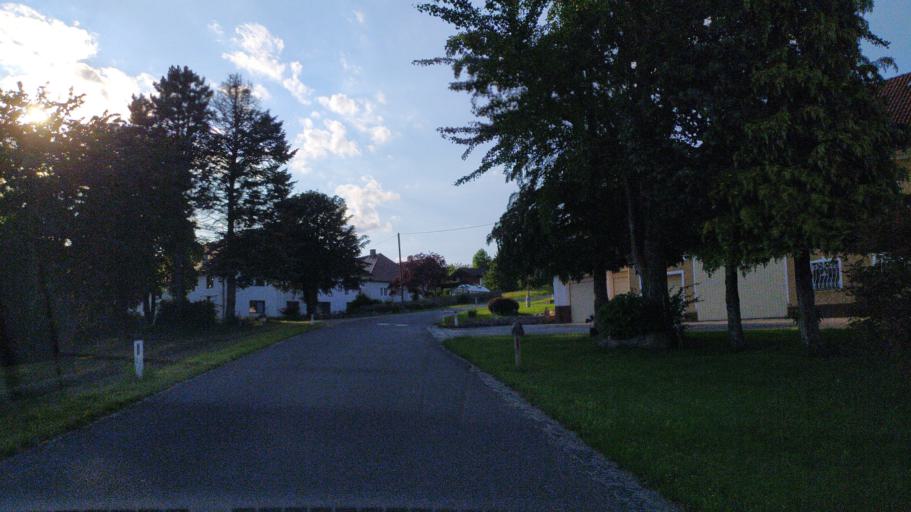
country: AT
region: Lower Austria
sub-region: Politischer Bezirk Amstetten
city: Strengberg
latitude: 48.1508
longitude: 14.6685
